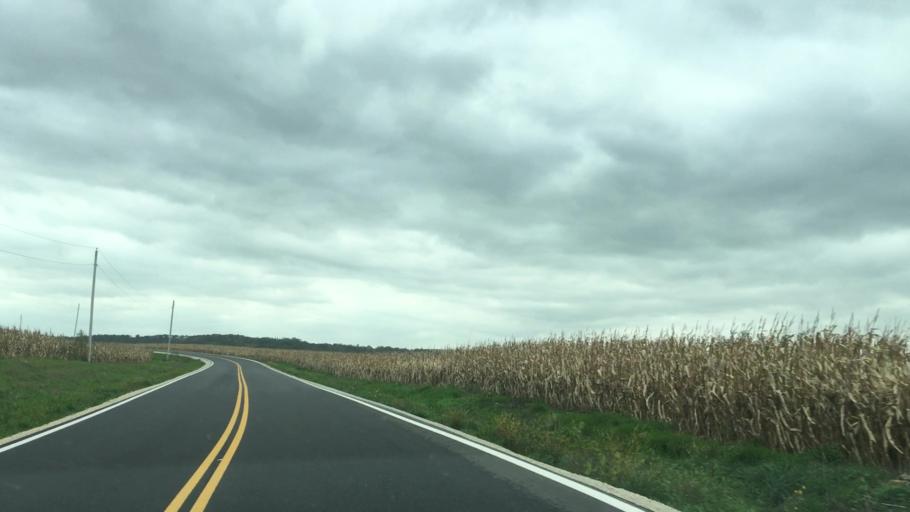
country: US
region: Minnesota
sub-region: Fillmore County
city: Preston
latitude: 43.7578
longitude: -92.0210
